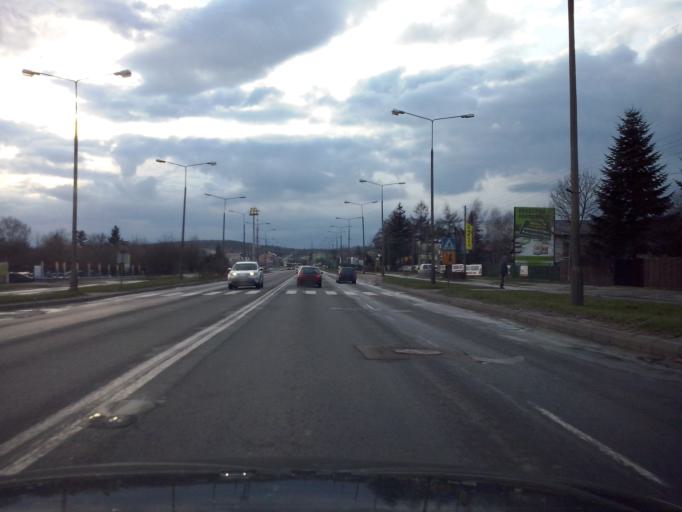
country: PL
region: Lublin Voivodeship
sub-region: Chelm
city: Chelm
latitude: 51.1459
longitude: 23.4435
